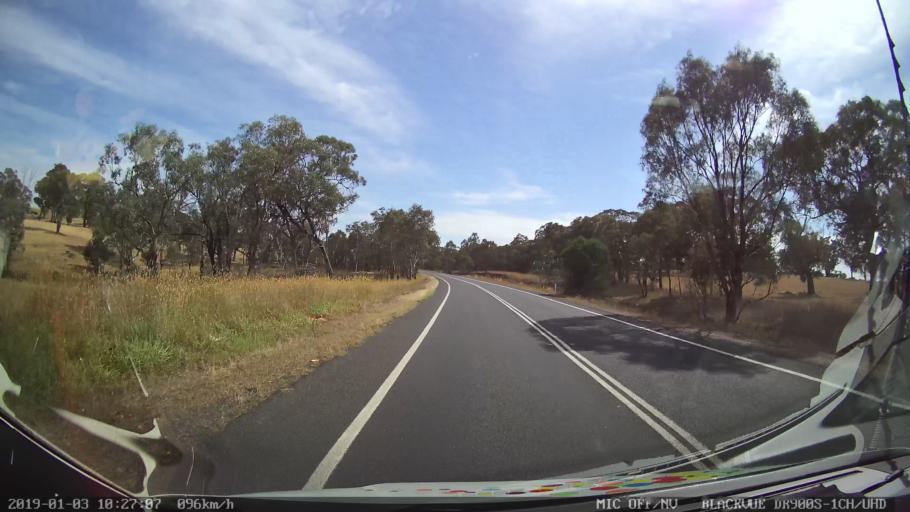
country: AU
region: New South Wales
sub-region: Young
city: Young
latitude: -34.4062
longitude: 148.2571
